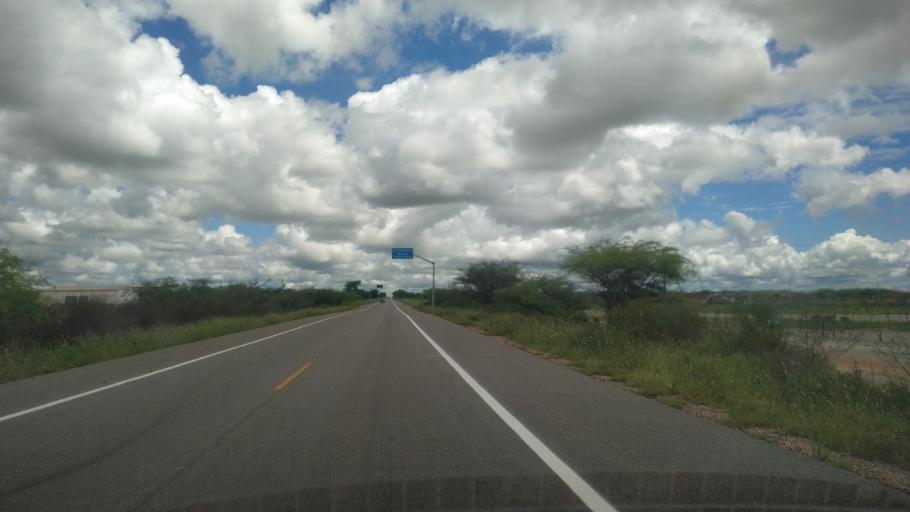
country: BR
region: Rio Grande do Norte
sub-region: Areia Branca
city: Areia Branca
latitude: -5.0535
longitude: -37.1516
